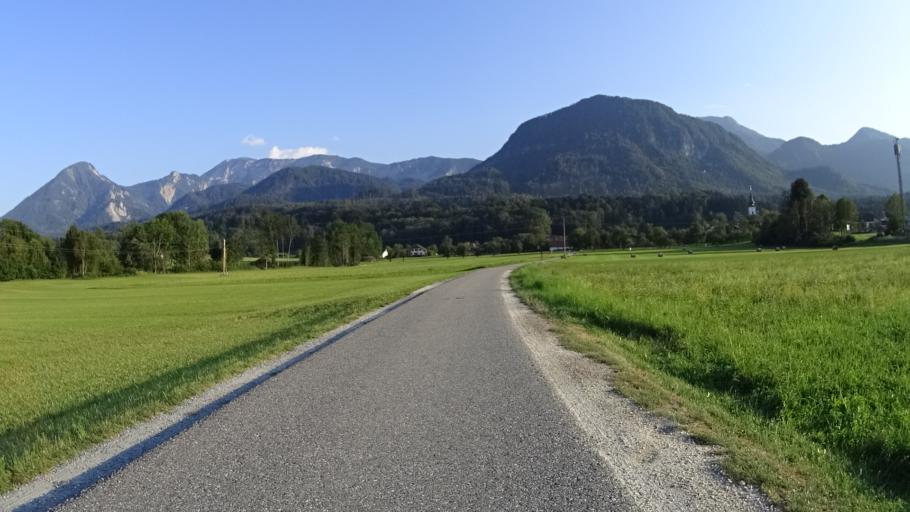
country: AT
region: Carinthia
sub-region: Politischer Bezirk Villach Land
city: Sankt Jakob
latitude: 46.5340
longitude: 14.0880
